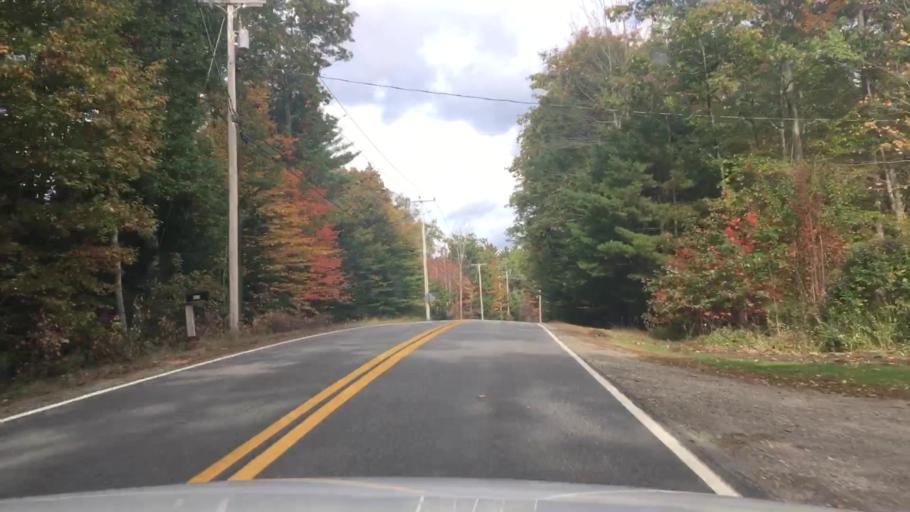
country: US
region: Maine
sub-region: Knox County
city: Hope
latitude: 44.3042
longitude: -69.1140
